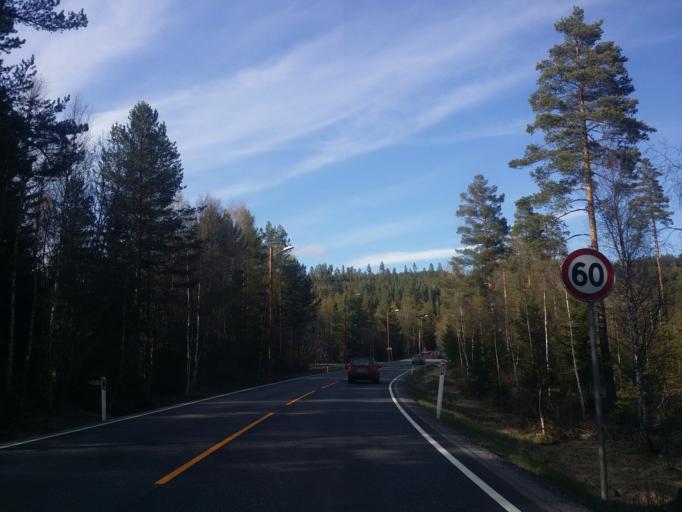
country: NO
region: Buskerud
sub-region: Kongsberg
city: Kongsberg
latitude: 59.6251
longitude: 9.4735
